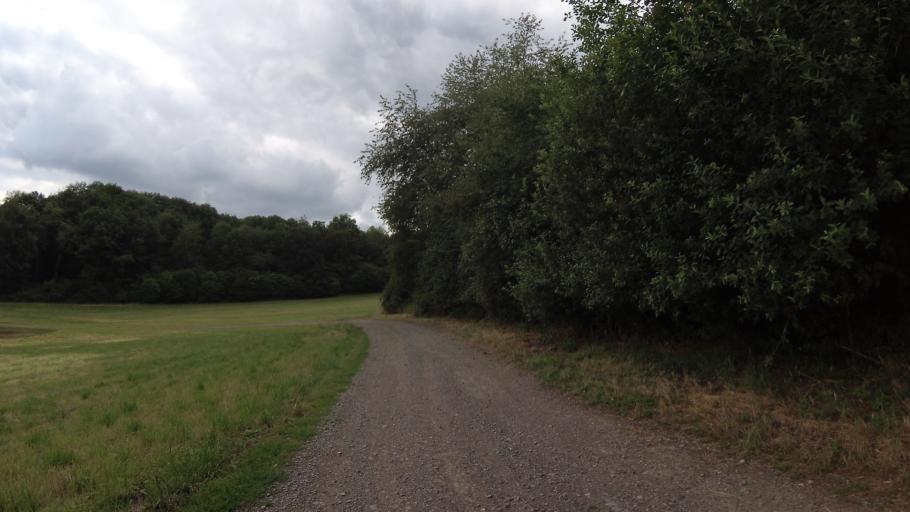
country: DE
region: Saarland
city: Sankt Wendel
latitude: 49.4997
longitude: 7.1861
